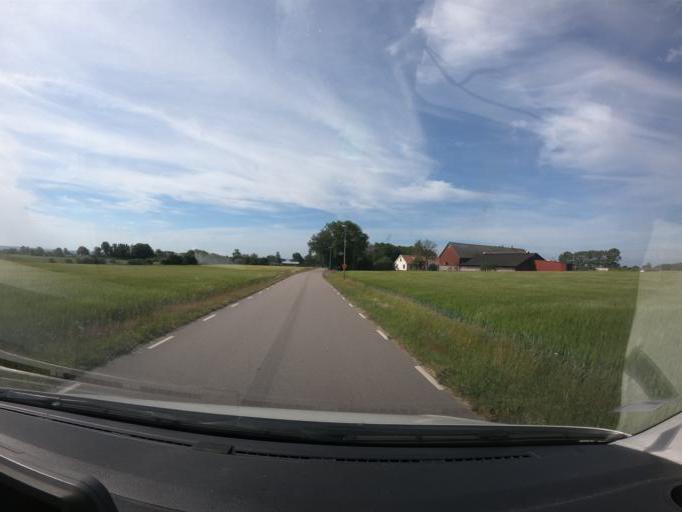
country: SE
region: Skane
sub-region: Angelholms Kommun
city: Vejbystrand
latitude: 56.3917
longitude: 12.6653
